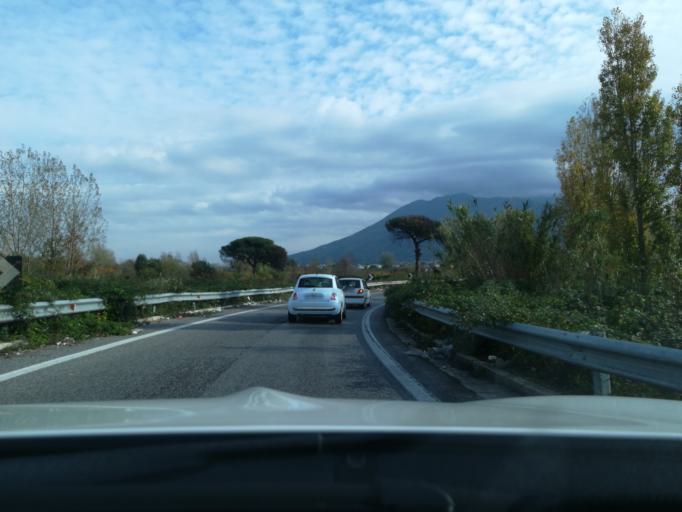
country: IT
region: Campania
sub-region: Provincia di Napoli
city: Cercola
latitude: 40.8698
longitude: 14.3597
